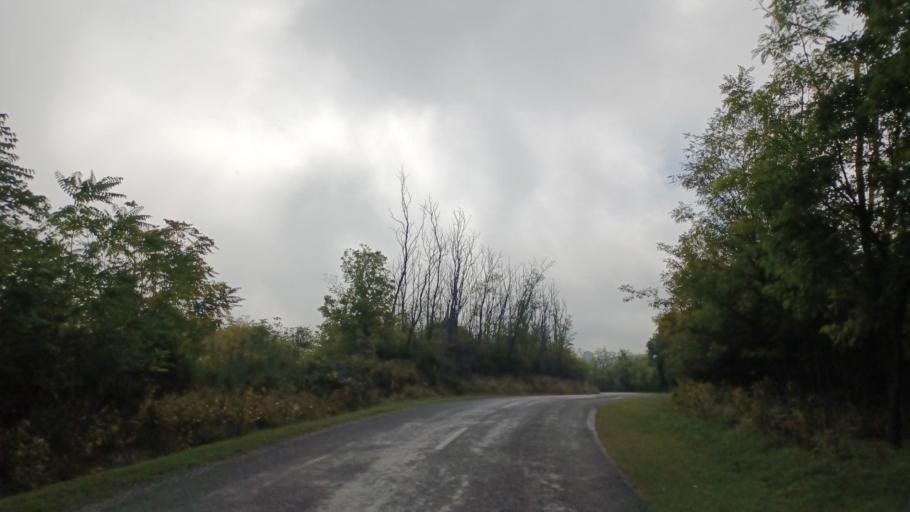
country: HU
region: Tolna
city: Pincehely
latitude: 46.6587
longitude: 18.5009
